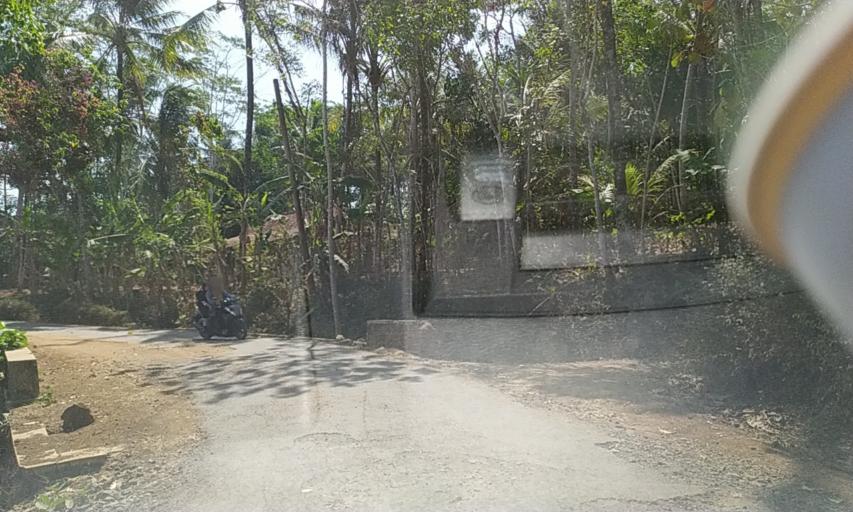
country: ID
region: Central Java
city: Rungkang
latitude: -7.4328
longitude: 108.8473
